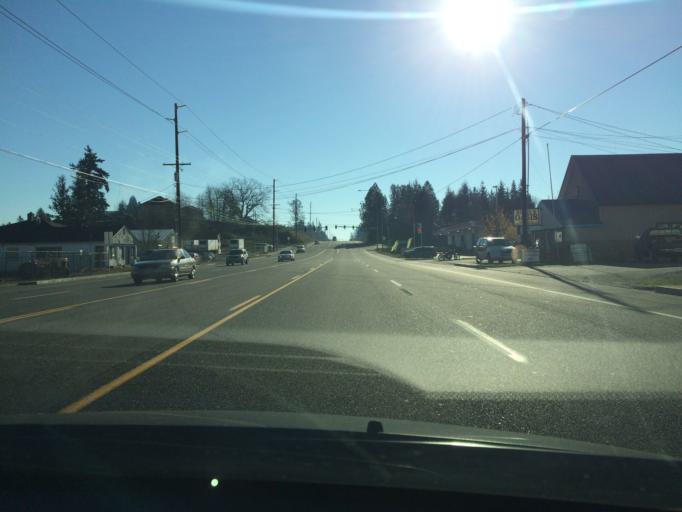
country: US
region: Washington
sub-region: Whatcom County
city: Marietta-Alderwood
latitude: 48.8570
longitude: -122.4860
